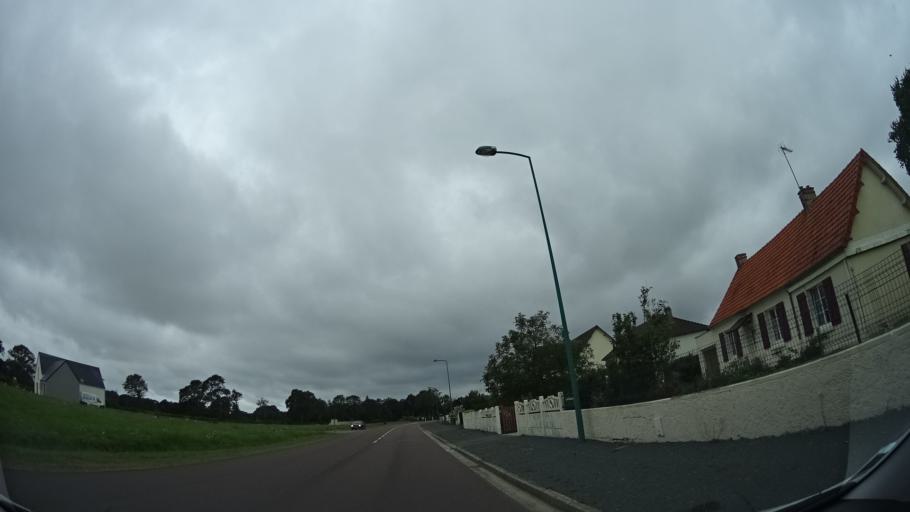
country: FR
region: Lower Normandy
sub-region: Departement de la Manche
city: La Haye-du-Puits
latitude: 49.3012
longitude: -1.5779
